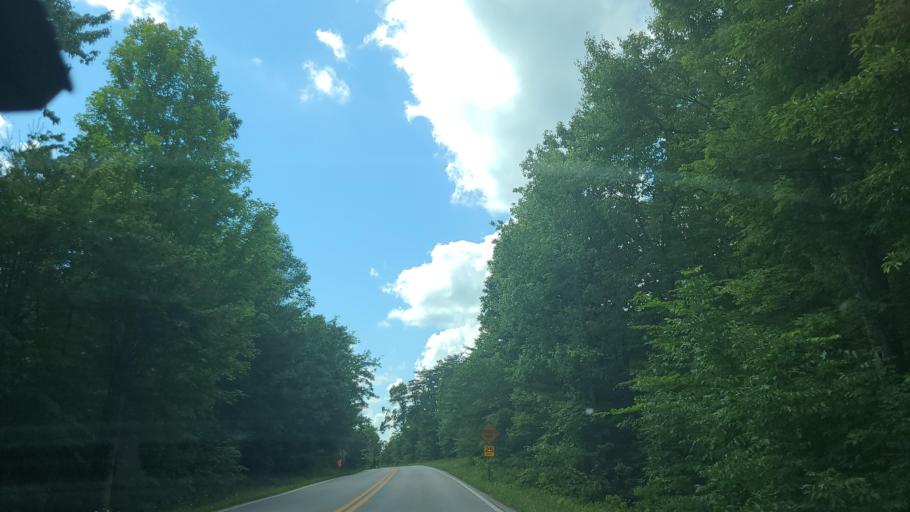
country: US
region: Kentucky
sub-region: Whitley County
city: Williamsburg
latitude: 36.8465
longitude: -84.3061
